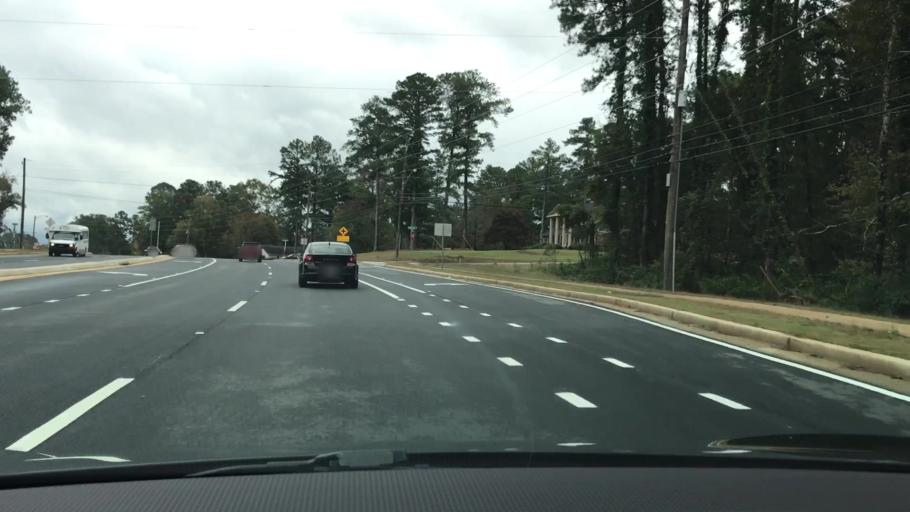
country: US
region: Georgia
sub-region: Oconee County
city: Watkinsville
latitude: 33.8809
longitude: -83.4542
